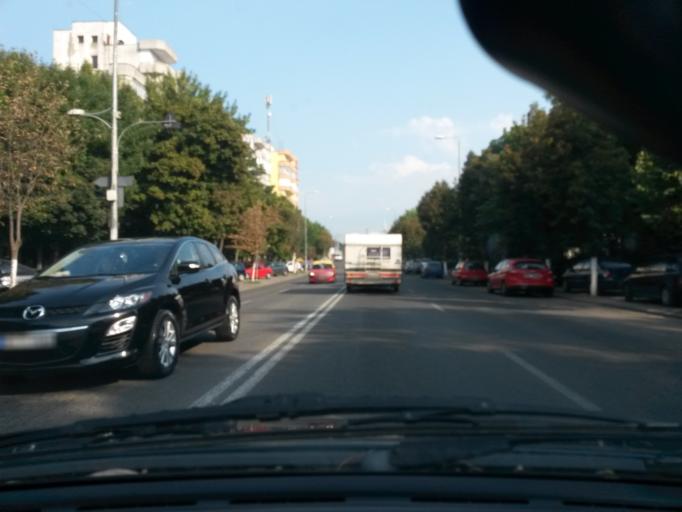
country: RO
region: Mures
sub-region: Comuna Corunca
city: Corunca
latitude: 46.5322
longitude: 24.5912
